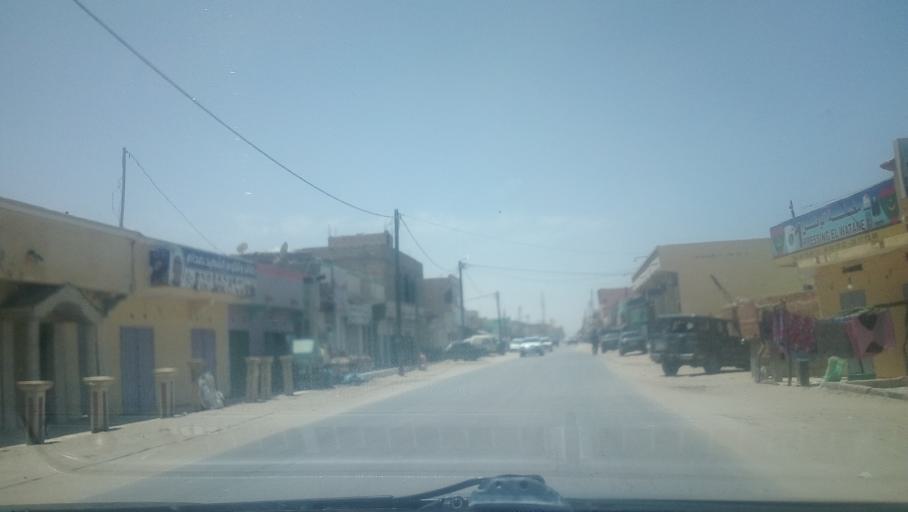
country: MR
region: Nouakchott
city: Nouakchott
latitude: 18.0665
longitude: -15.9587
